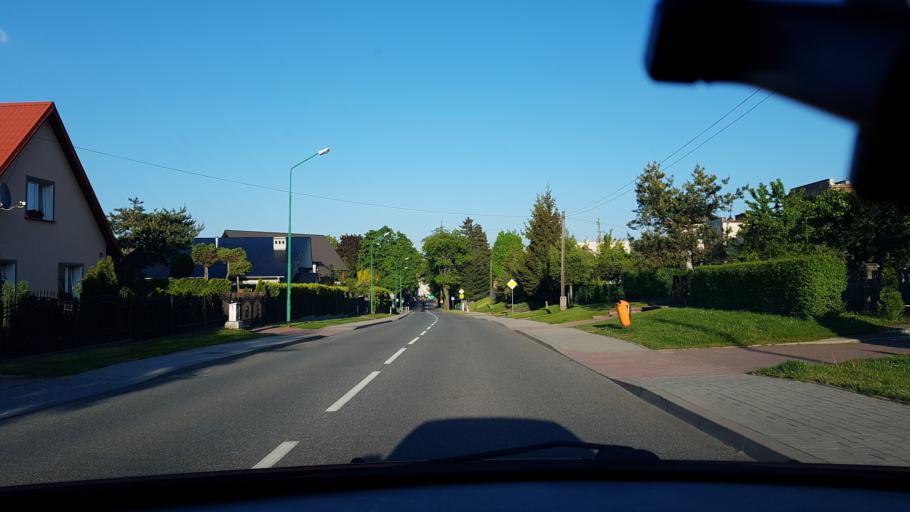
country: PL
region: Lower Silesian Voivodeship
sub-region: Powiat zabkowicki
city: Zabkowice Slaskie
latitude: 50.5906
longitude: 16.8002
